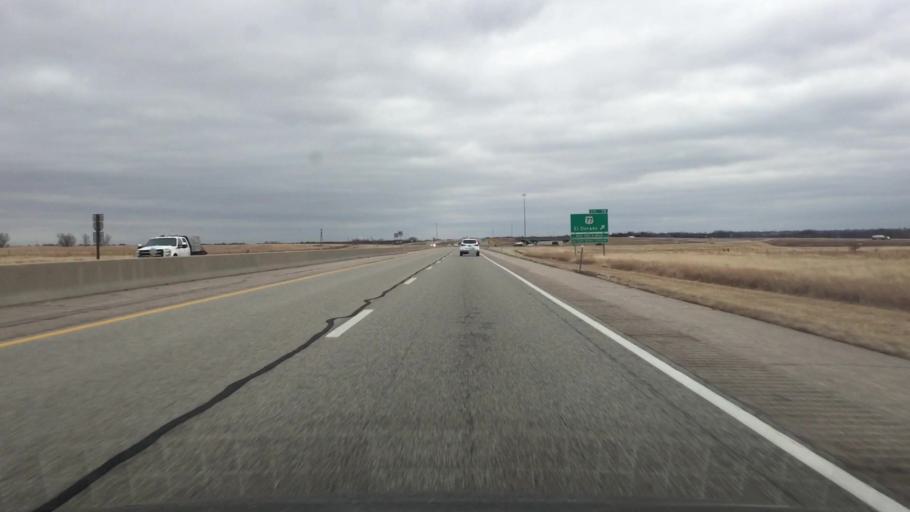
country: US
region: Kansas
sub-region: Butler County
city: El Dorado
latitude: 37.8820
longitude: -96.8422
